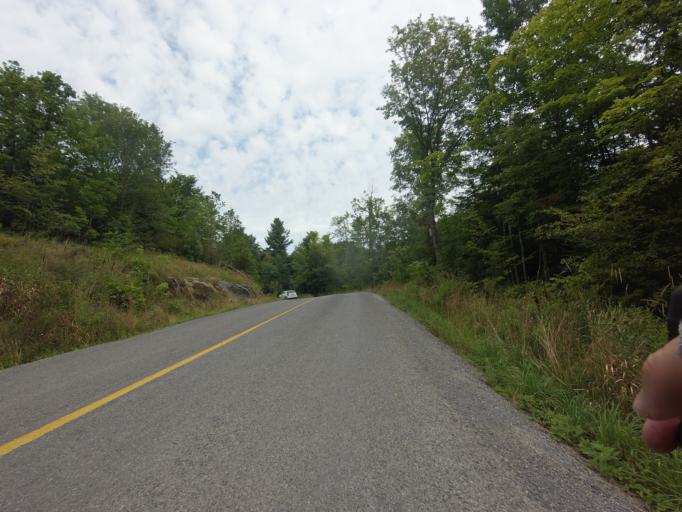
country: CA
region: Ontario
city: Perth
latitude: 44.6740
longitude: -76.6599
